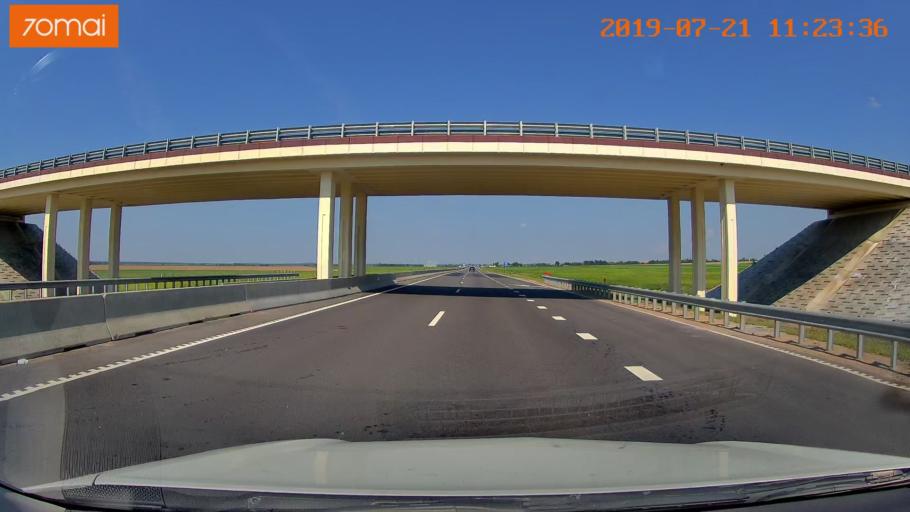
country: BY
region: Minsk
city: Valozhyn
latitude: 54.0476
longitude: 26.5632
